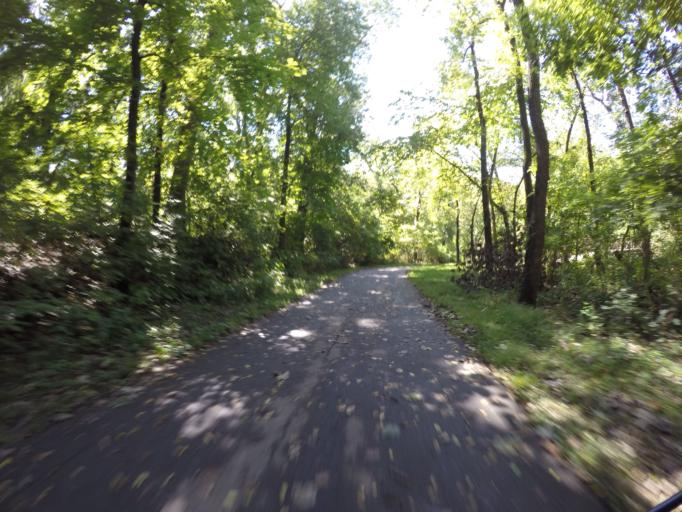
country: US
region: Kansas
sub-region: Johnson County
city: Lenexa
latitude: 38.9023
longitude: -94.7339
